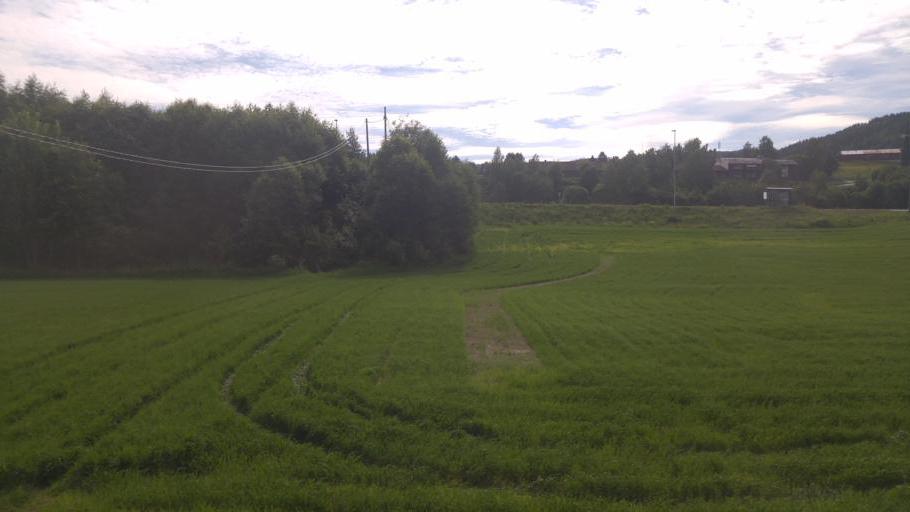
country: NO
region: Sor-Trondelag
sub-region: Melhus
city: Lundamo
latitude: 63.1367
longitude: 10.2515
